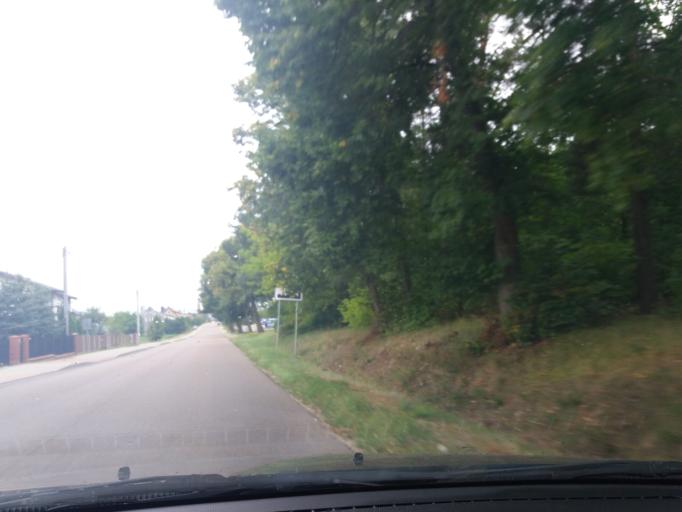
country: PL
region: Masovian Voivodeship
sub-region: Powiat mlawski
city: Wieczfnia Koscielna
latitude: 53.1990
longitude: 20.4865
